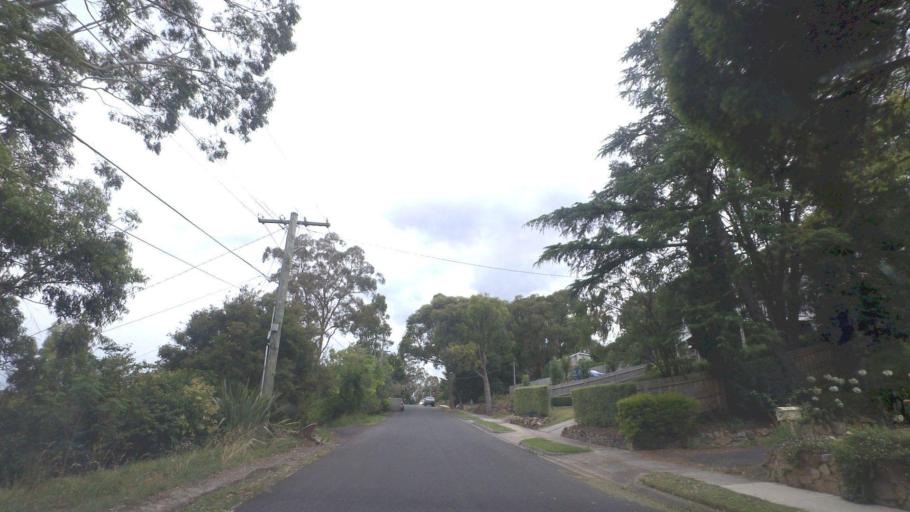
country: AU
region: Victoria
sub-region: Yarra Ranges
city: Lilydale
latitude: -37.7572
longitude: 145.3644
